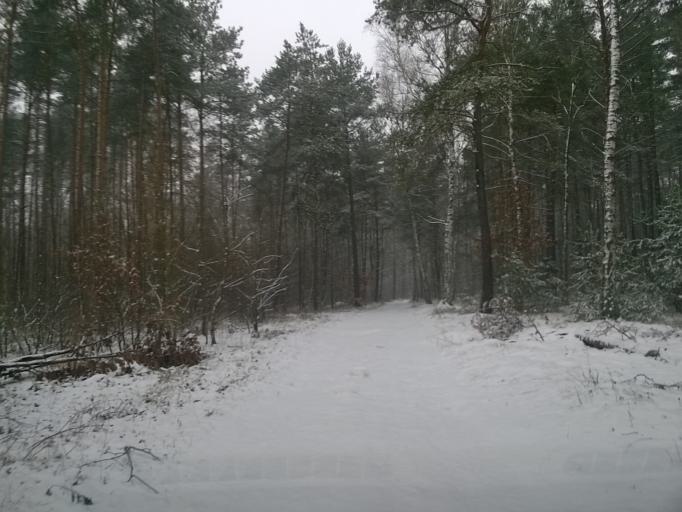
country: PL
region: Kujawsko-Pomorskie
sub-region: Powiat swiecki
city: Swiecie
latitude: 53.4201
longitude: 18.3903
